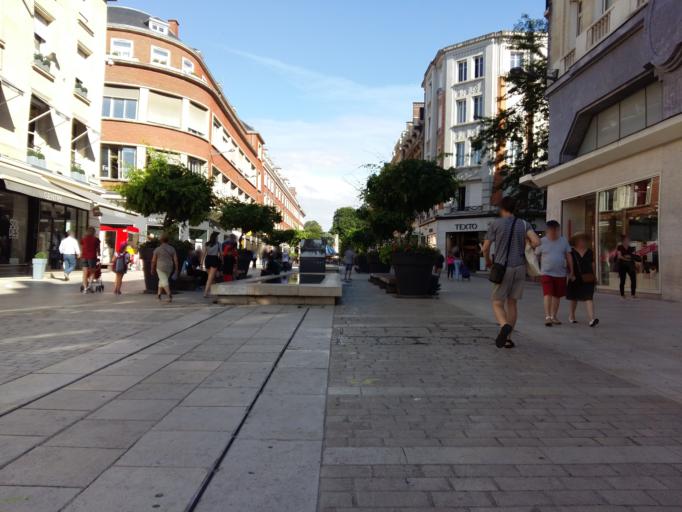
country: FR
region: Picardie
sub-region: Departement de la Somme
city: Amiens
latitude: 49.8926
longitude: 2.2996
